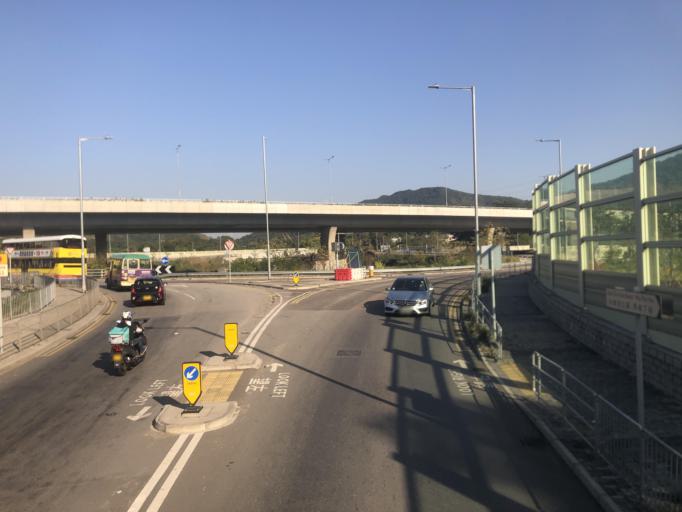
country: CN
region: Guangdong
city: Liantang
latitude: 22.5214
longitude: 114.1784
